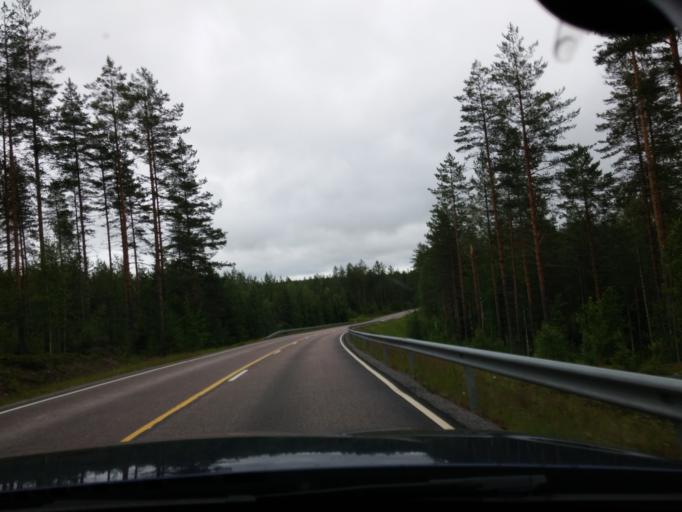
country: FI
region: Central Finland
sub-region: Saarijaervi-Viitasaari
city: Pylkoenmaeki
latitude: 62.5924
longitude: 24.5993
